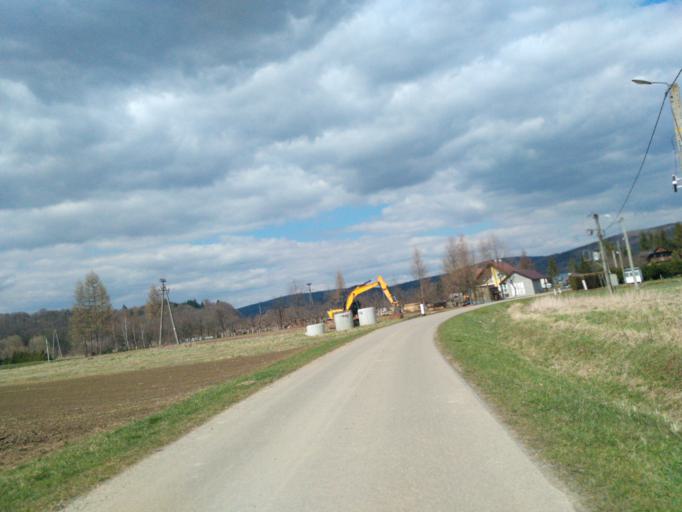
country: PL
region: Subcarpathian Voivodeship
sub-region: Powiat sanocki
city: Tyrawa Woloska
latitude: 49.6430
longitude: 22.2977
